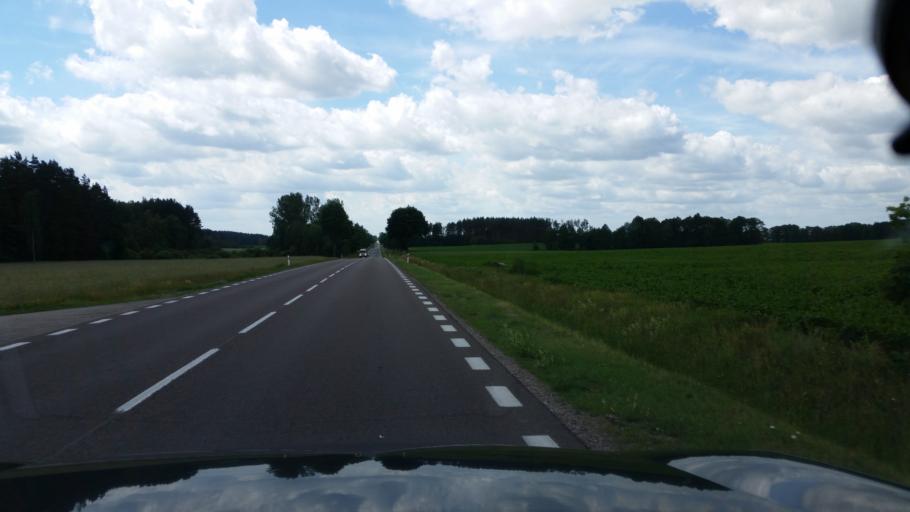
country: PL
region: Podlasie
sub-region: Powiat kolnenski
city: Stawiski
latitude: 53.4760
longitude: 22.2100
